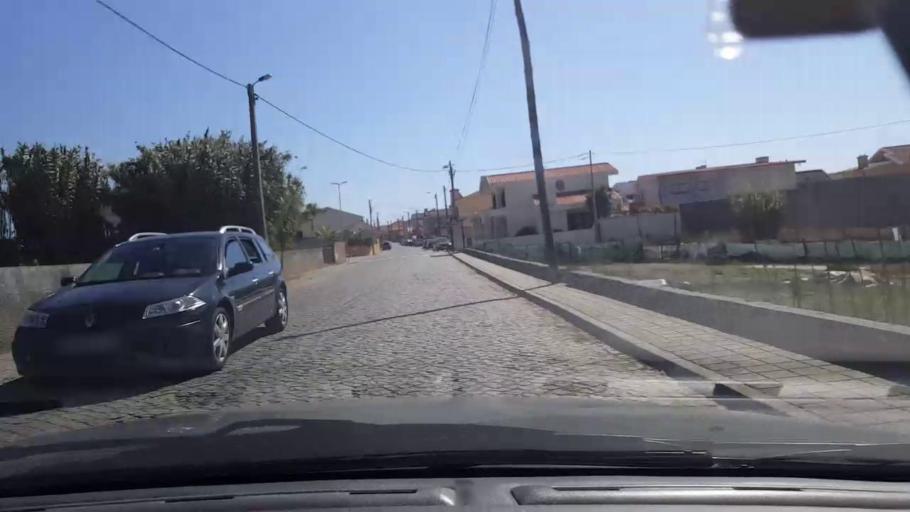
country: PT
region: Porto
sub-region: Vila do Conde
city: Arvore
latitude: 41.2998
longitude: -8.7348
